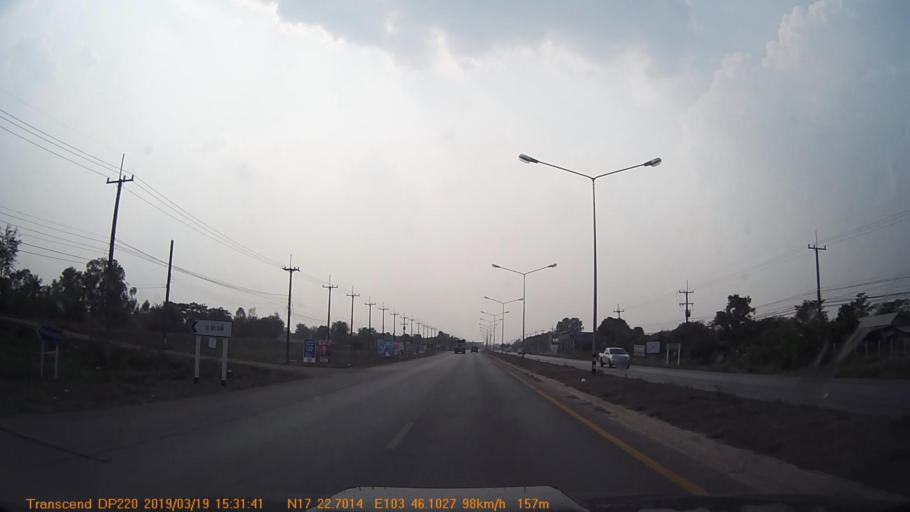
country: TH
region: Sakon Nakhon
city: Phang Khon
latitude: 17.3784
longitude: 103.7680
